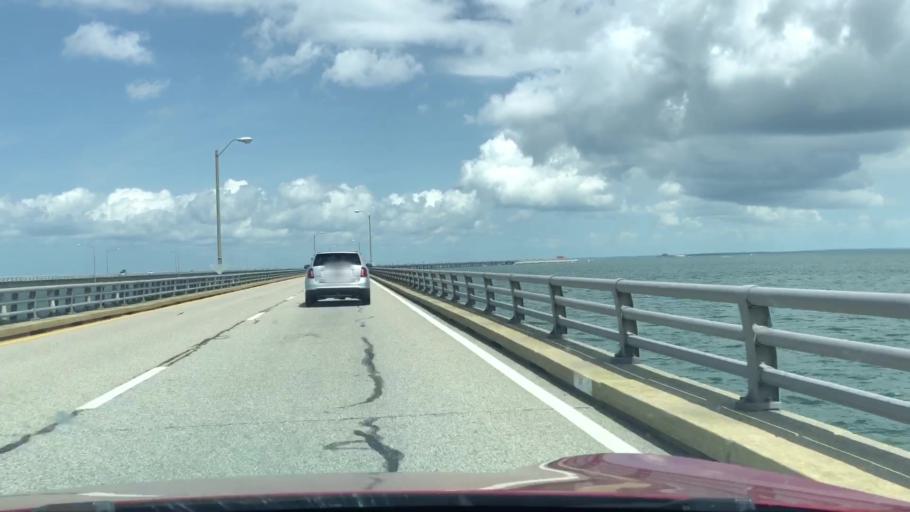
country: US
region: Virginia
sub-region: City of Virginia Beach
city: Virginia Beach
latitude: 37.0182
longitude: -76.0911
